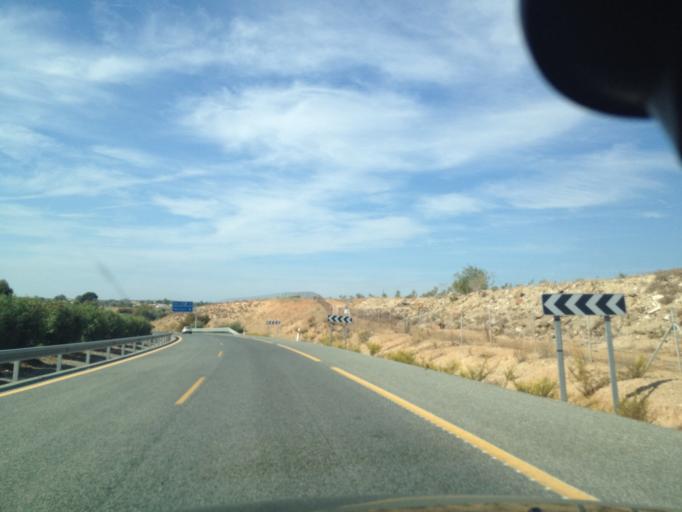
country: ES
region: Andalusia
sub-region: Provincia de Sevilla
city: La Puebla de Cazalla
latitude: 37.2341
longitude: -5.3121
